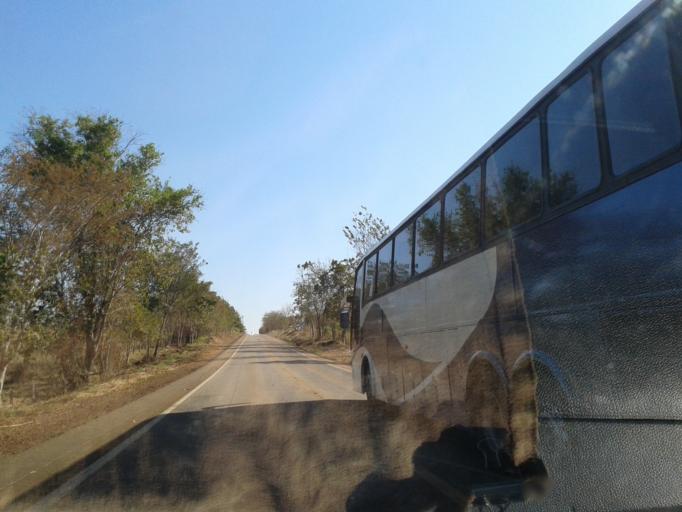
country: BR
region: Goias
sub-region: Mozarlandia
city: Mozarlandia
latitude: -14.7368
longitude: -50.5442
